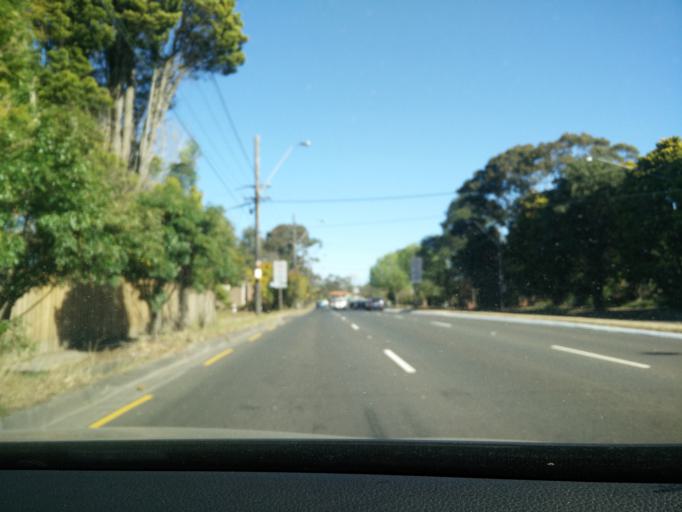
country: AU
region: New South Wales
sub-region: City of Sydney
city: Pymble
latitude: -33.7654
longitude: 151.1369
